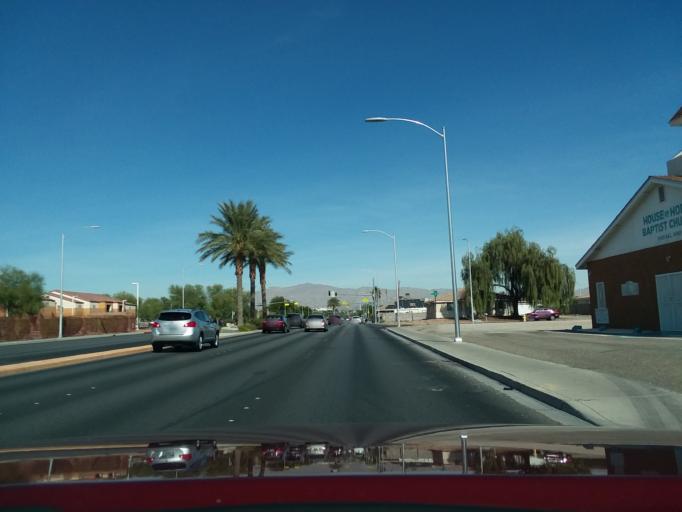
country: US
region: Nevada
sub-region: Clark County
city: Las Vegas
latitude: 36.1978
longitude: -115.1607
